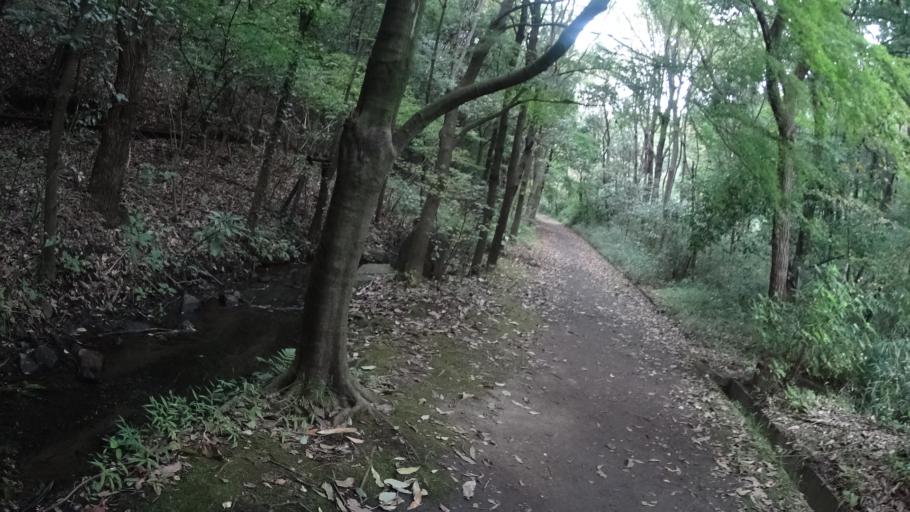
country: JP
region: Kanagawa
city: Zushi
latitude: 35.3553
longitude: 139.5991
